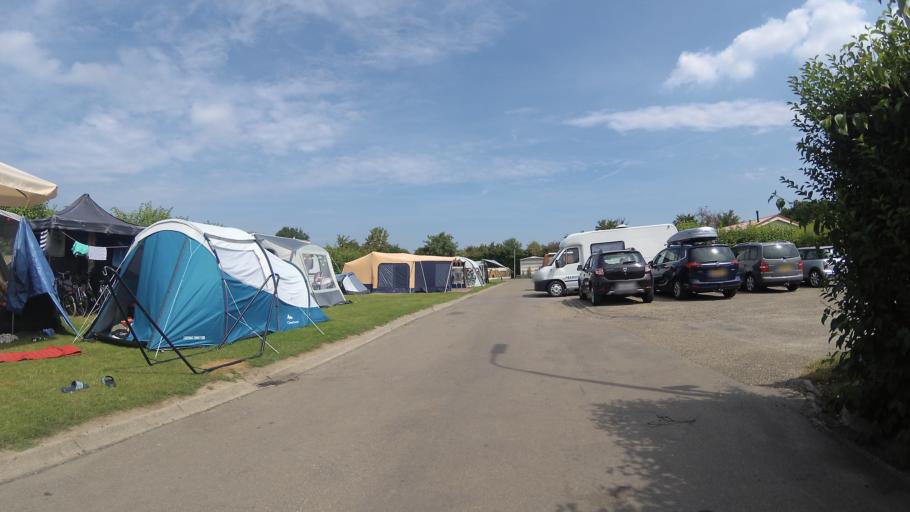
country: NL
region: Zeeland
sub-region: Gemeente Noord-Beveland
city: Kamperland
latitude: 51.5897
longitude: 3.7291
